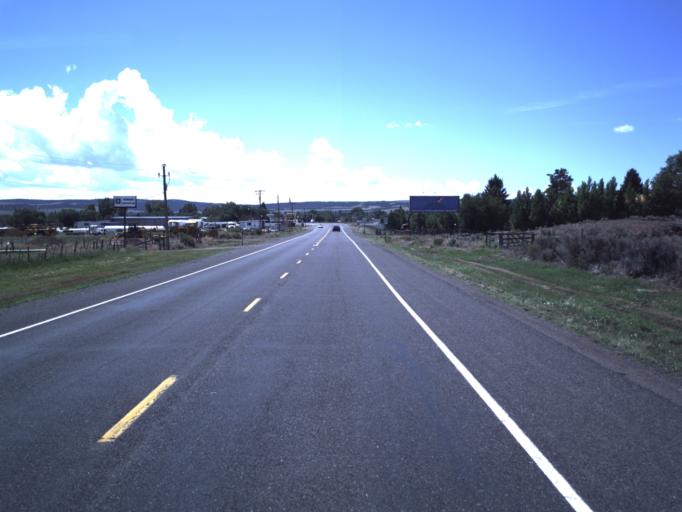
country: US
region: Utah
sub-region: Garfield County
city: Panguitch
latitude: 37.8405
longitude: -112.4385
